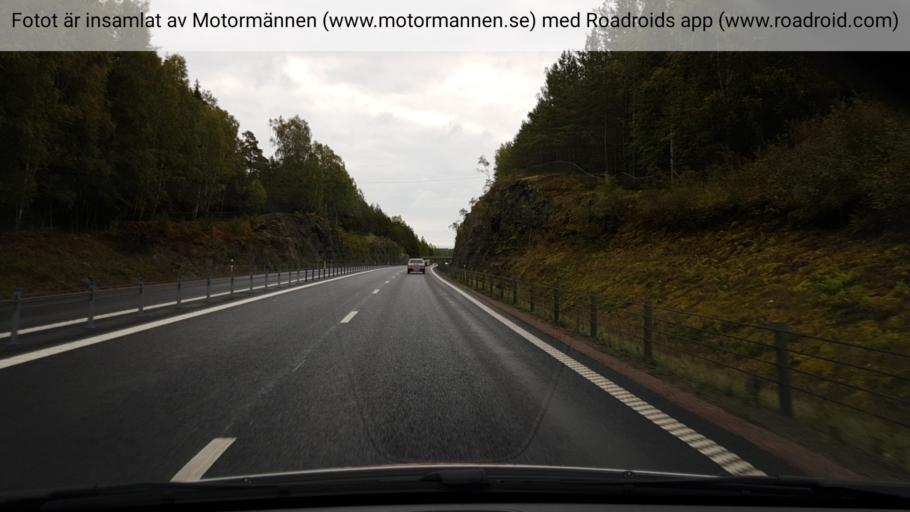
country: SE
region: Vaermland
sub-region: Karlstads Kommun
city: Skattkarr
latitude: 59.4175
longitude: 13.7296
